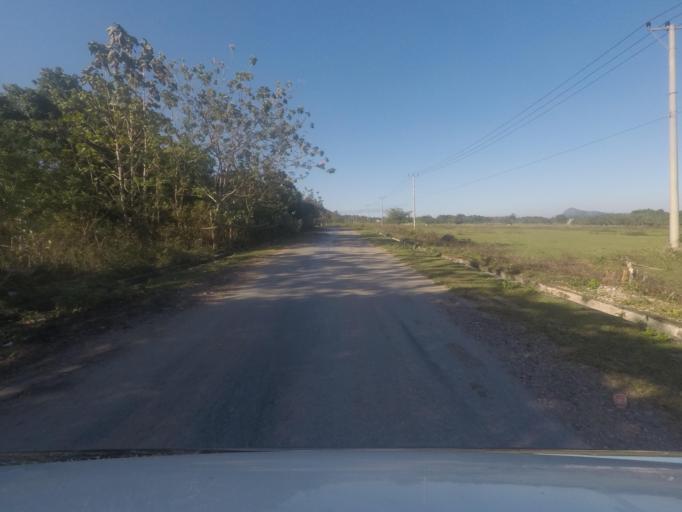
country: TL
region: Lautem
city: Lospalos
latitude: -8.4058
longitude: 127.1745
